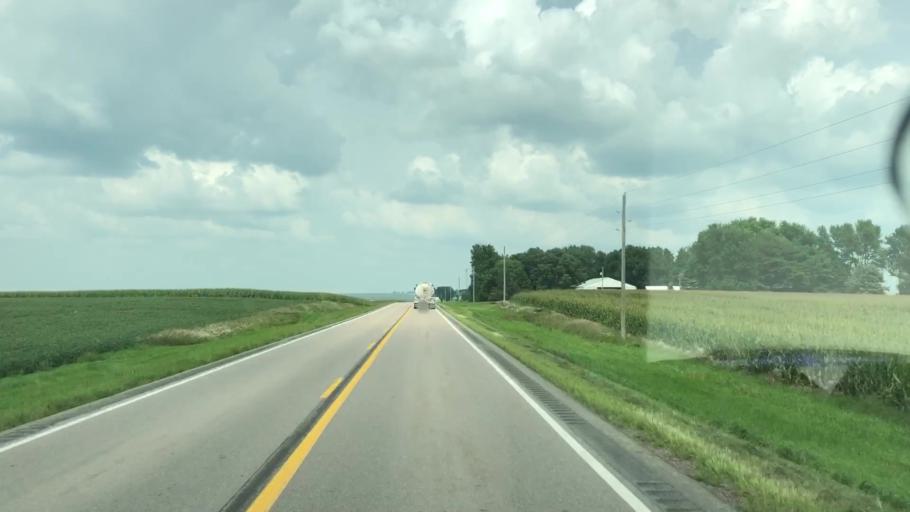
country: US
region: Iowa
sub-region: Plymouth County
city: Remsen
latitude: 42.7958
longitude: -95.9577
